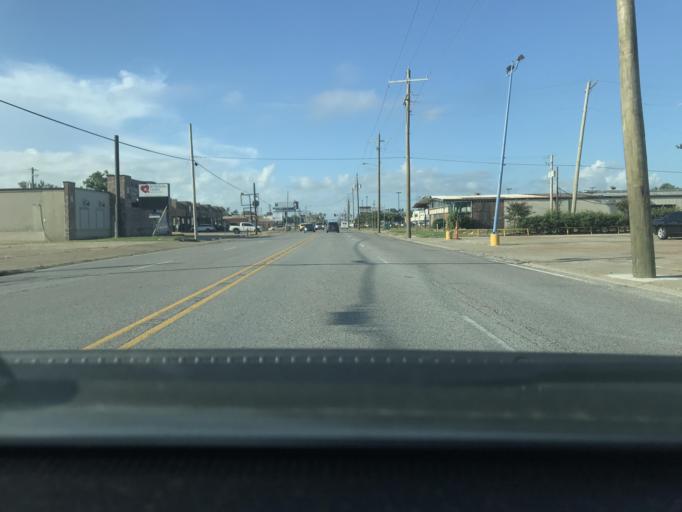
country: US
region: Louisiana
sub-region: Calcasieu Parish
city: Lake Charles
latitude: 30.2077
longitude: -93.2187
